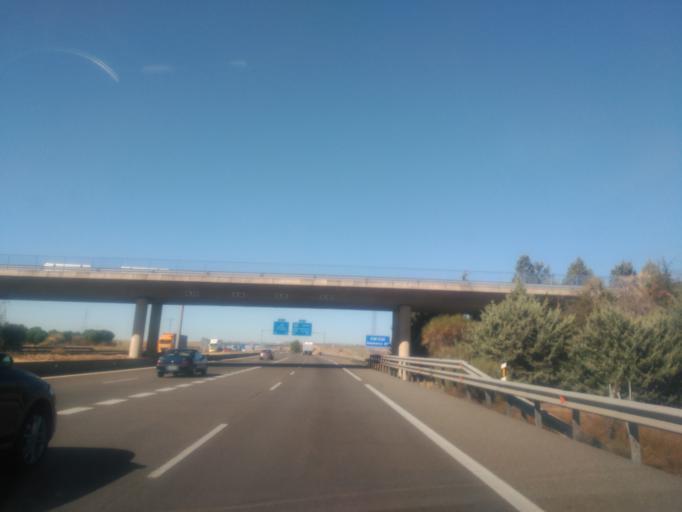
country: ES
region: Castille and Leon
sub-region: Provincia de Valladolid
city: Tordesillas
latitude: 41.5107
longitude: -4.9917
